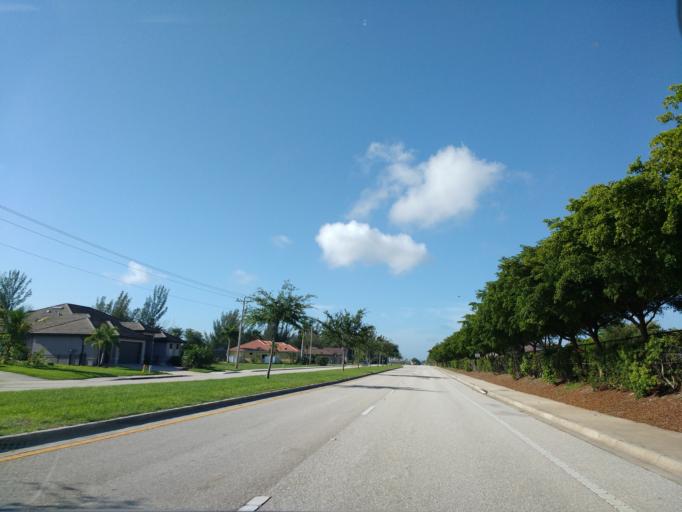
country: US
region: Florida
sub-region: Lee County
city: Cape Coral
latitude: 26.6134
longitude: -82.0235
